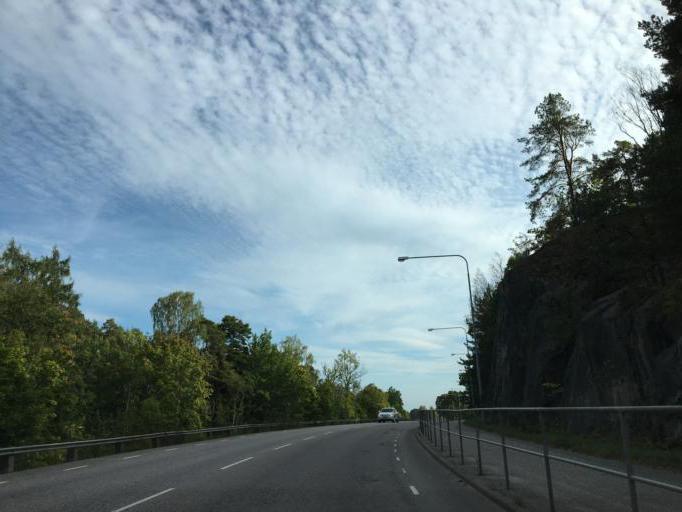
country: SE
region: Soedermanland
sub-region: Eskilstuna Kommun
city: Torshalla
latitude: 59.4216
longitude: 16.4604
